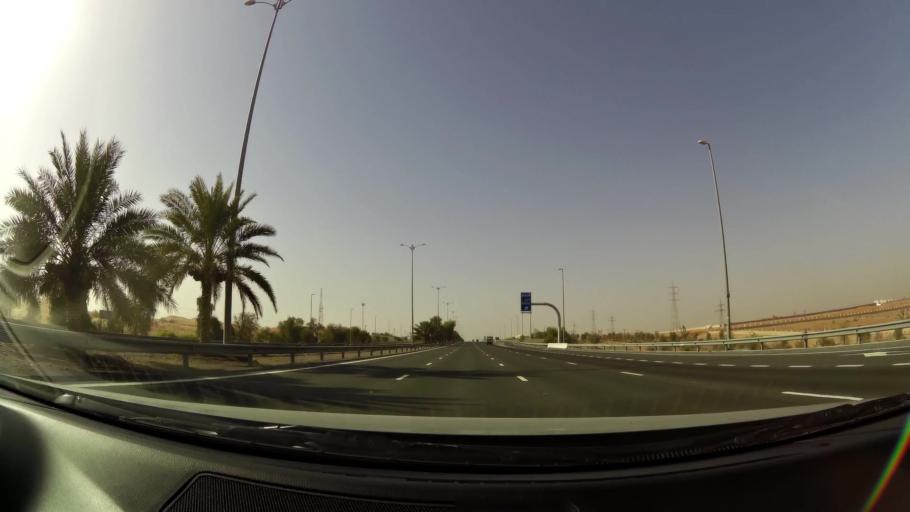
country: OM
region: Al Buraimi
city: Al Buraymi
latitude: 24.4945
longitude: 55.7702
